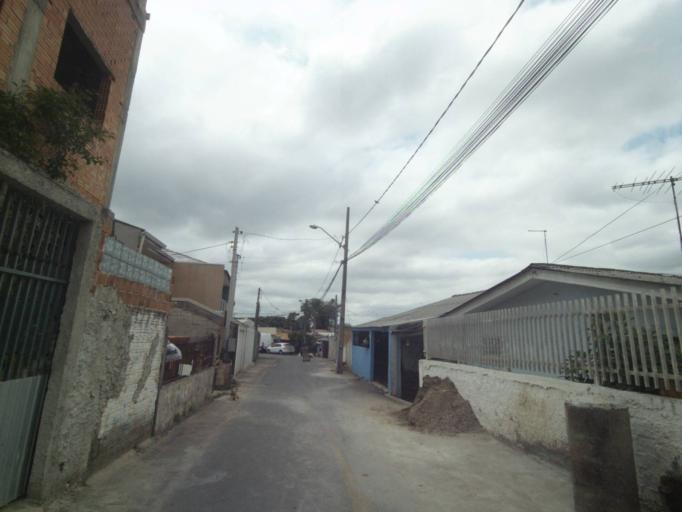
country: BR
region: Parana
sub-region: Sao Jose Dos Pinhais
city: Sao Jose dos Pinhais
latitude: -25.5375
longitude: -49.2670
